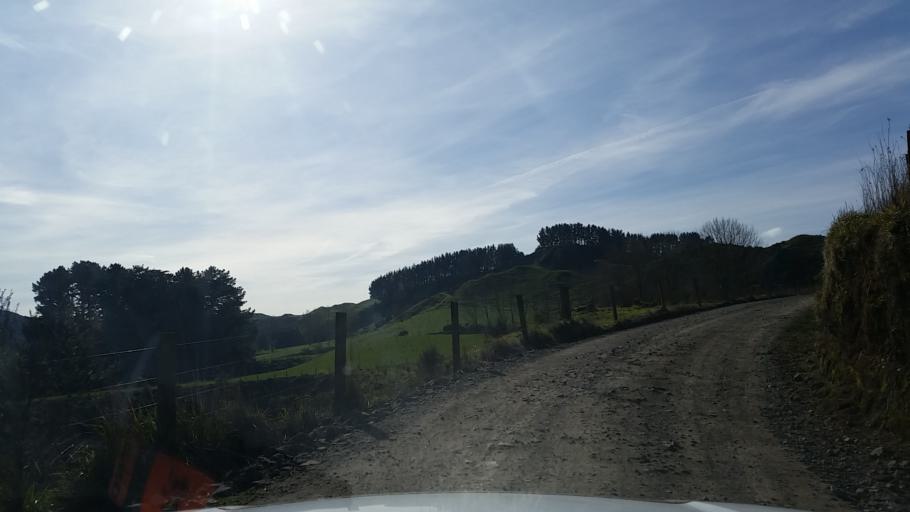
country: NZ
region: Taranaki
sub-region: South Taranaki District
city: Eltham
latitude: -39.3561
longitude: 174.5117
